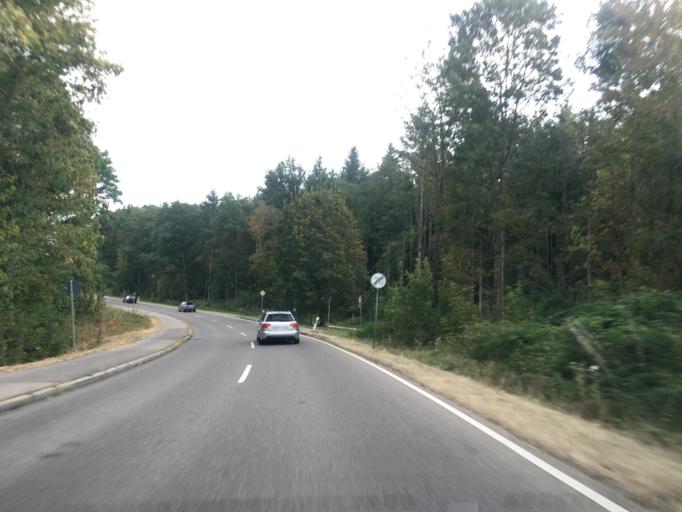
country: DE
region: Baden-Wuerttemberg
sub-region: Tuebingen Region
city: Wannweil
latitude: 48.4731
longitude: 9.1536
